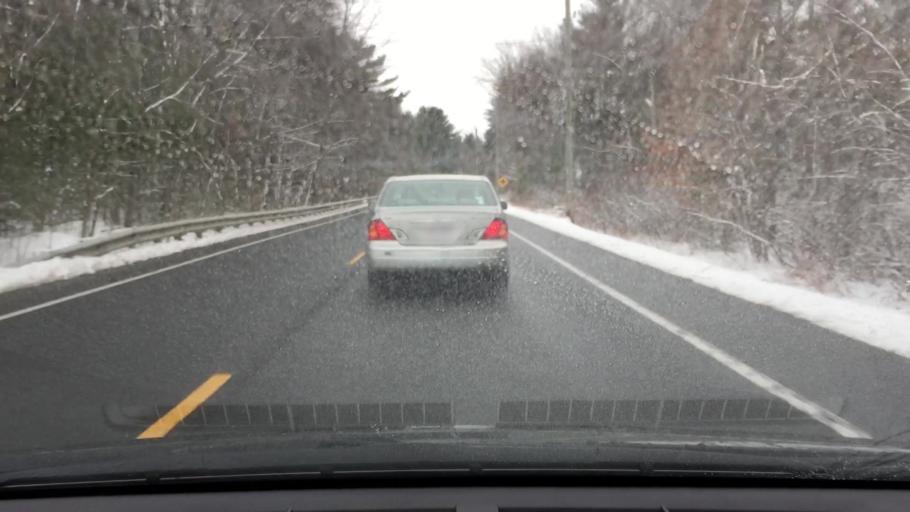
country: US
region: Massachusetts
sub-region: Hampshire County
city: Pelham
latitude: 42.3532
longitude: -72.4027
